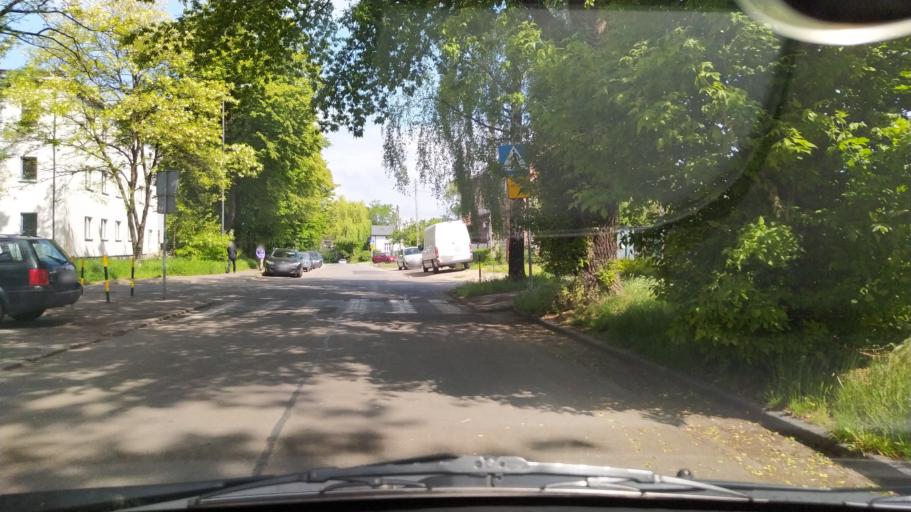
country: PL
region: Silesian Voivodeship
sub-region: Powiat gliwicki
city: Przyszowice
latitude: 50.2876
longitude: 18.7297
